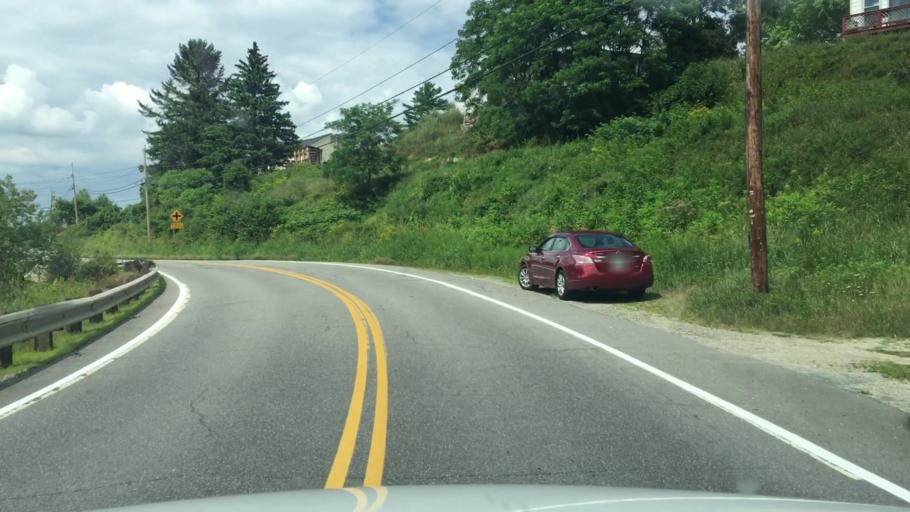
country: US
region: New Hampshire
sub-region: Grafton County
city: Deerfield
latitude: 44.2942
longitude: -71.6576
